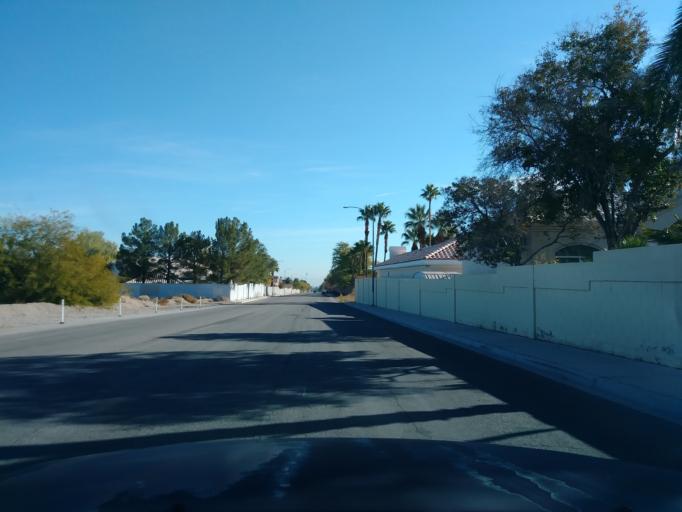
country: US
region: Nevada
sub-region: Clark County
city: Spring Valley
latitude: 36.1477
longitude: -115.2768
